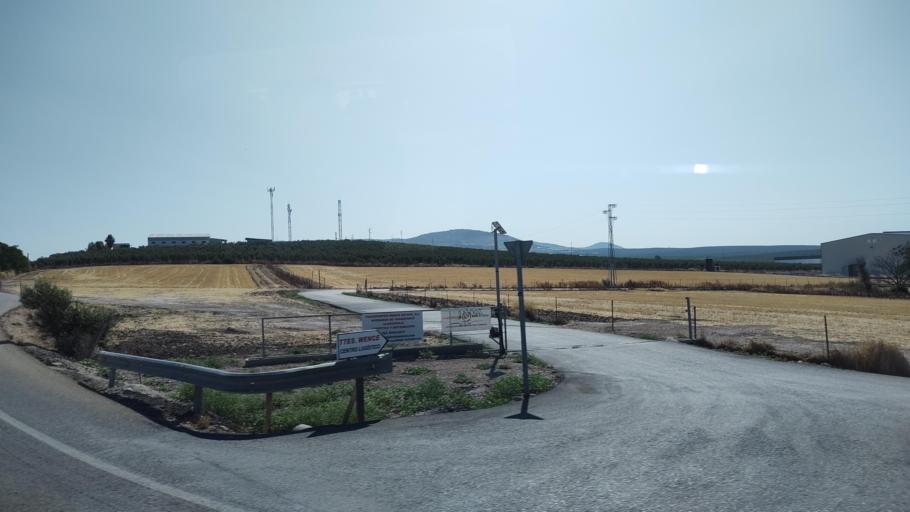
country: ES
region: Andalusia
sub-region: Provincia de Sevilla
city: Aguadulce
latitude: 37.2564
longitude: -4.9842
